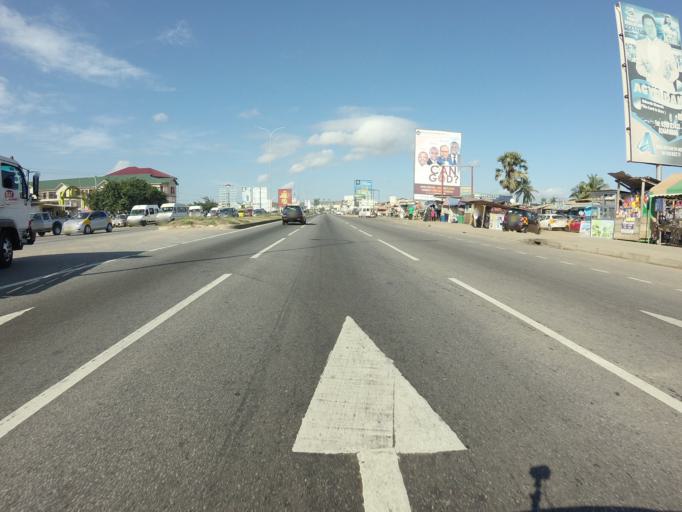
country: GH
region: Greater Accra
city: Gbawe
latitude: 5.5477
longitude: -0.3381
